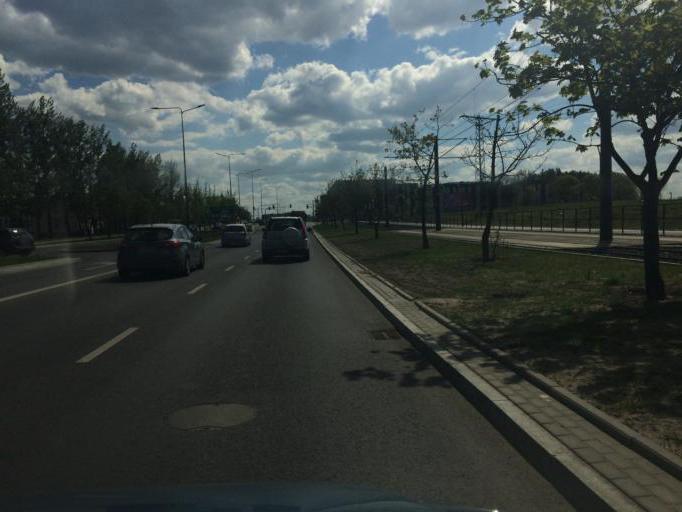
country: PL
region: Warmian-Masurian Voivodeship
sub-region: Powiat olsztynski
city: Olsztyn
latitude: 53.7581
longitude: 20.4865
